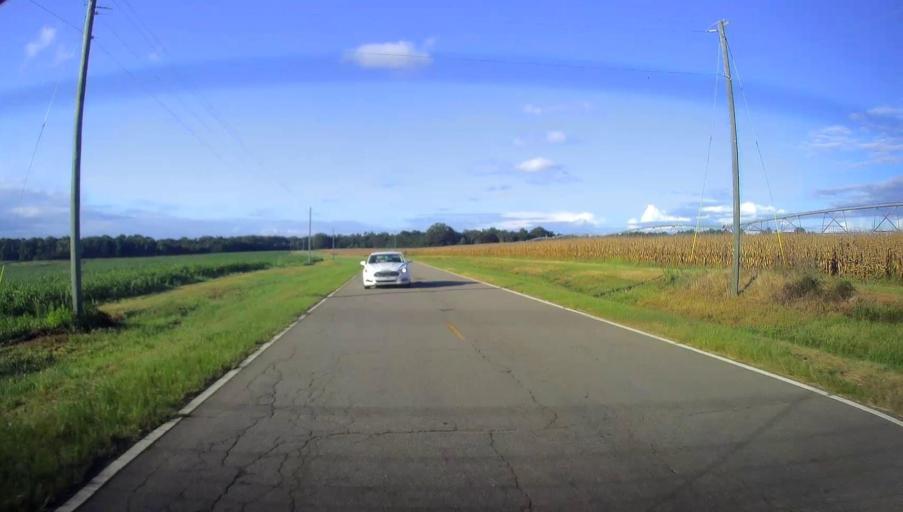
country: US
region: Georgia
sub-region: Pulaski County
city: Hawkinsville
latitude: 32.3786
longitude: -83.4600
